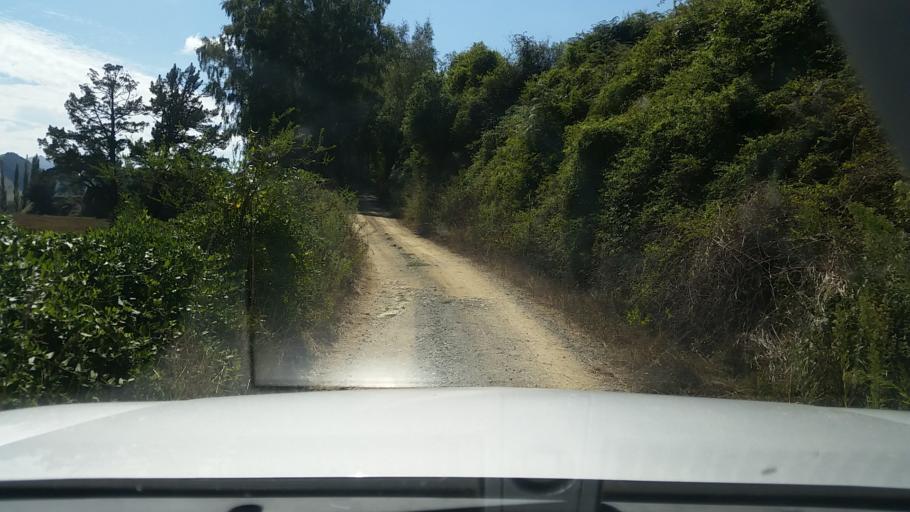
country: NZ
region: Nelson
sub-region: Nelson City
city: Nelson
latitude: -41.2498
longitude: 173.5843
